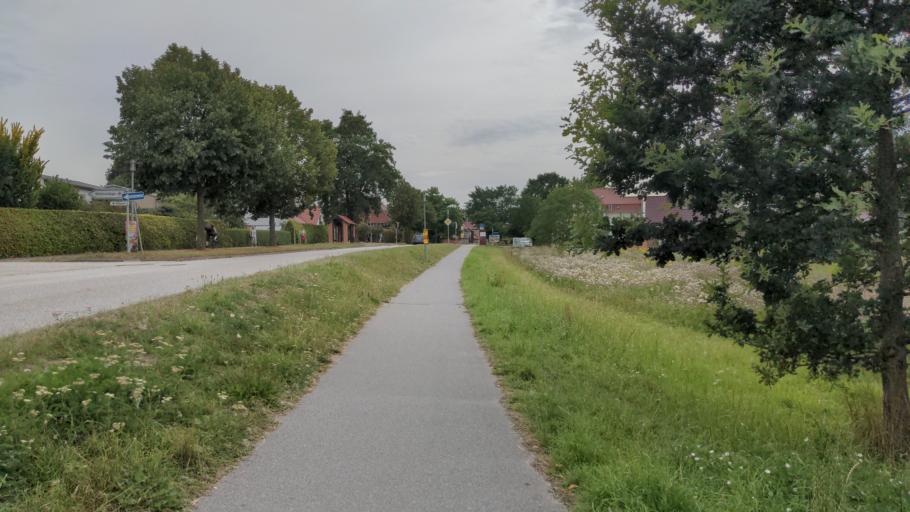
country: DE
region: Mecklenburg-Vorpommern
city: Klutz
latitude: 53.9679
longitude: 11.1710
